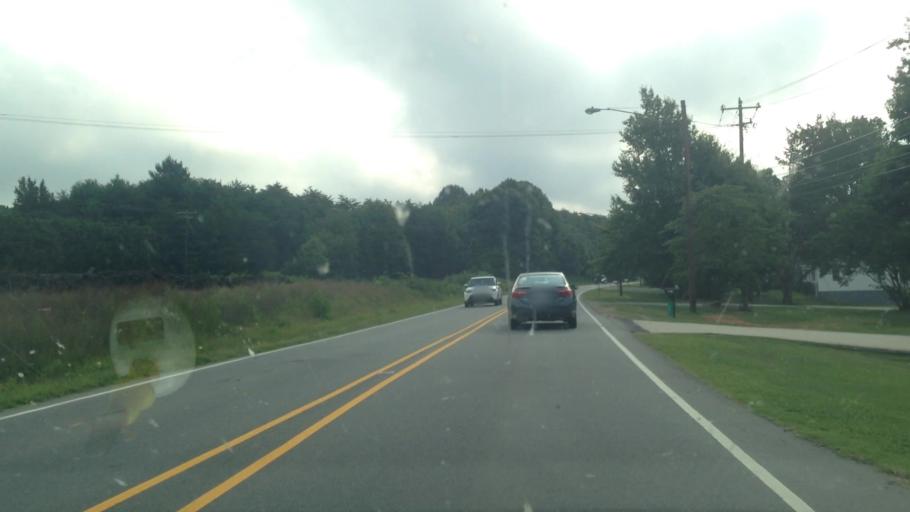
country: US
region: North Carolina
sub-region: Forsyth County
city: Kernersville
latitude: 36.1367
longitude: -80.1085
